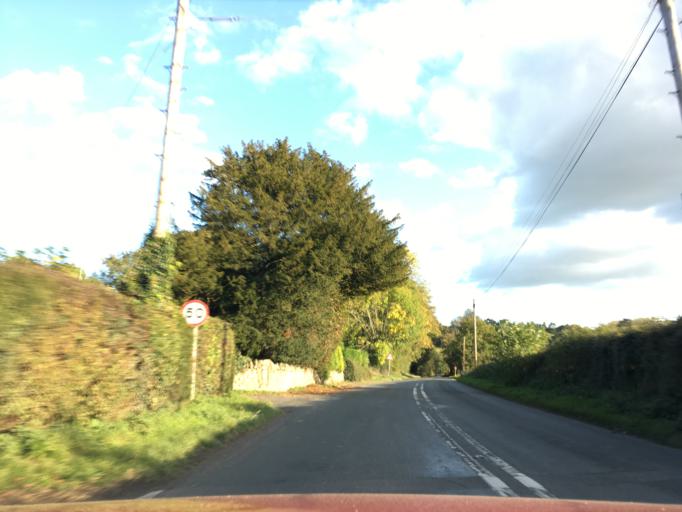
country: GB
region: England
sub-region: Herefordshire
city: Donnington
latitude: 52.0297
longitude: -2.3775
